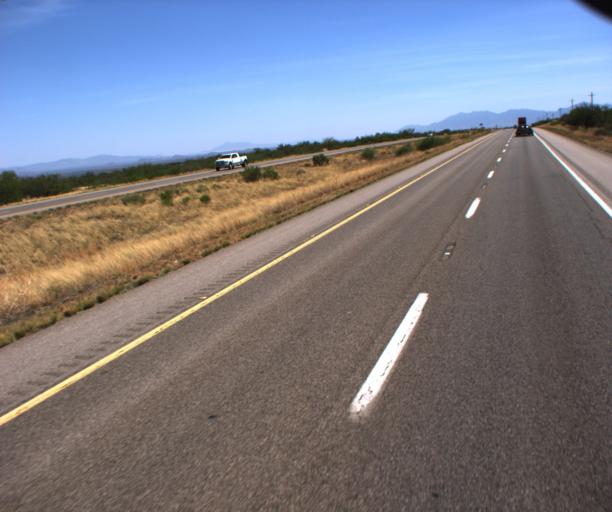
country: US
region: Arizona
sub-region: Cochise County
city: Whetstone
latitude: 31.8624
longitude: -110.3413
